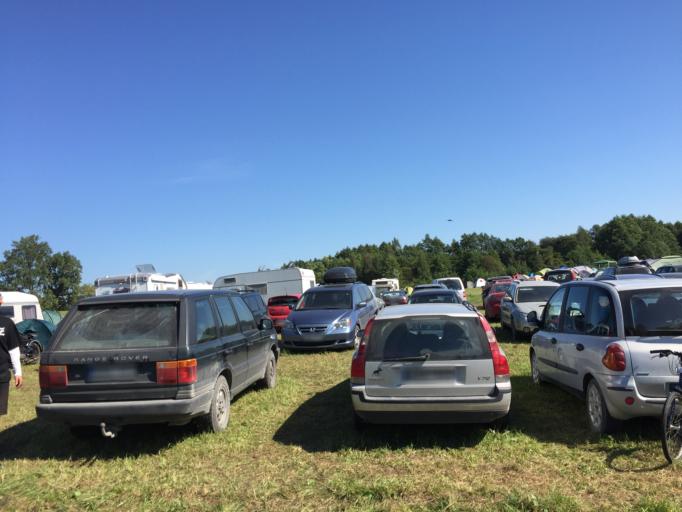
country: LT
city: Zarasai
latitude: 55.7863
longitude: 25.9626
